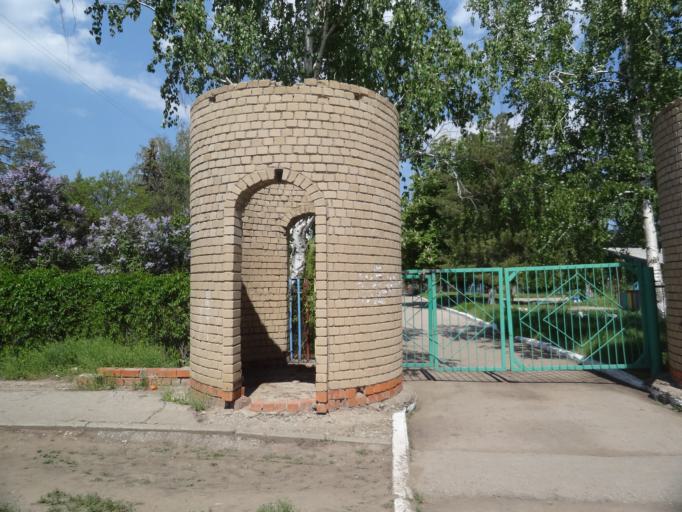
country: RU
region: Saratov
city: Privolzhskiy
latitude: 51.3914
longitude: 46.1240
